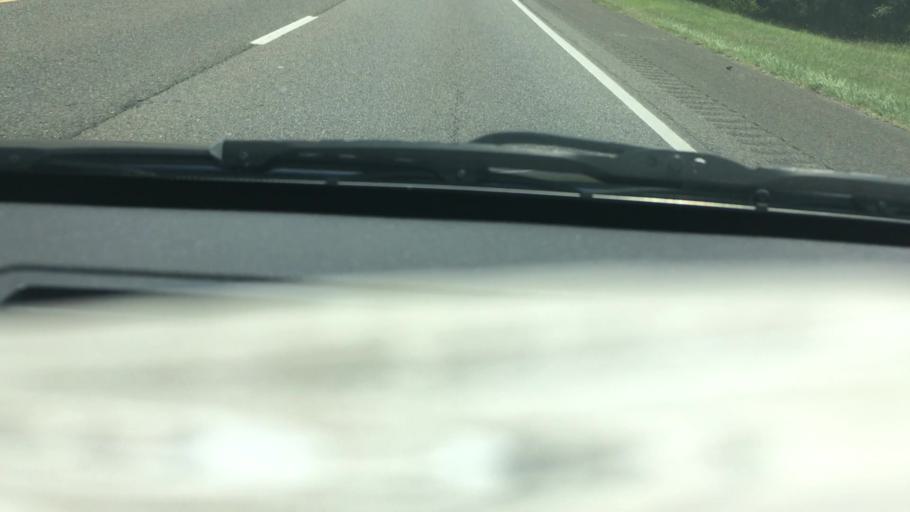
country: US
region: Alabama
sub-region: Pickens County
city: Gordo
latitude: 33.2784
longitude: -87.7764
